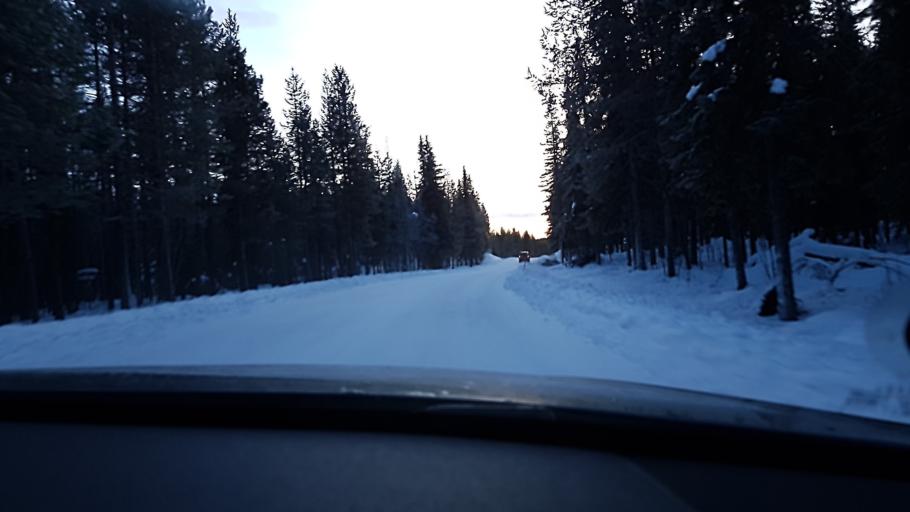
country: SE
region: Vaesterbotten
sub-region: Sorsele Kommun
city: Sorsele
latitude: 65.4975
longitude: 17.5570
